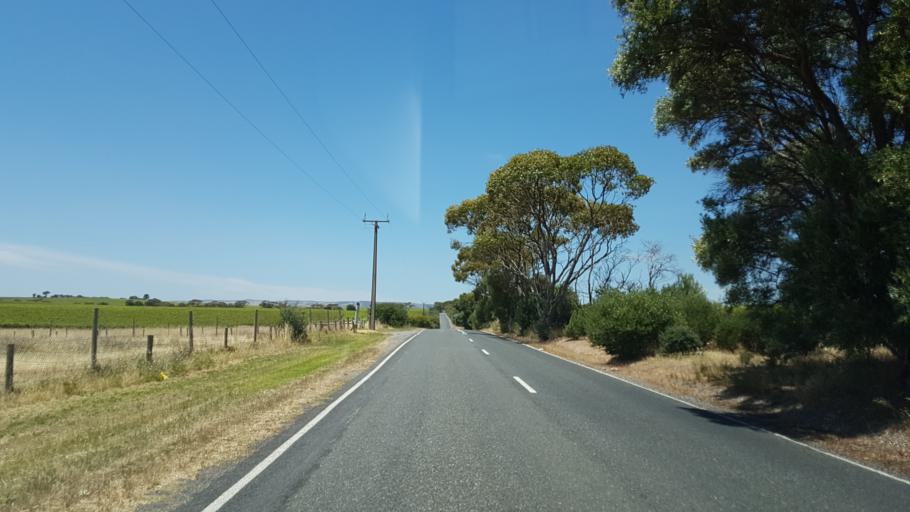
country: AU
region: South Australia
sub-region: Onkaparinga
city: Moana
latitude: -35.2323
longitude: 138.4977
